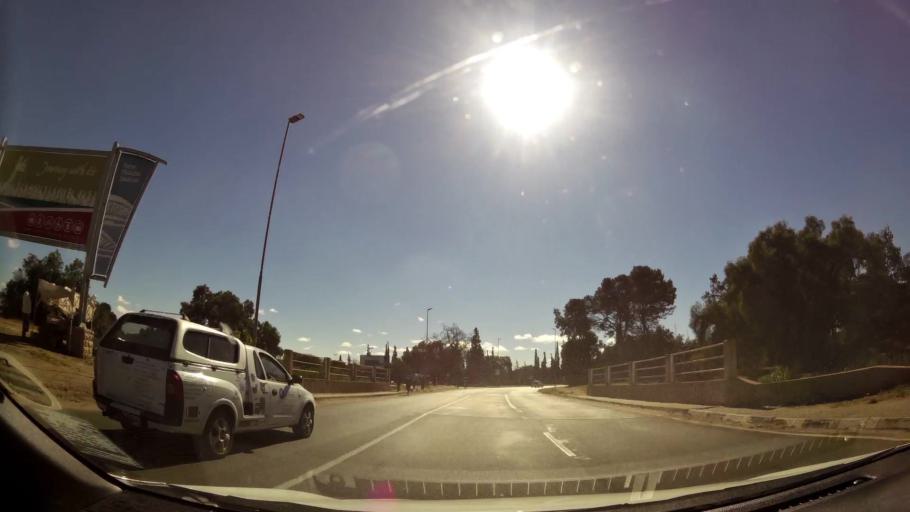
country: ZA
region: Limpopo
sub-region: Capricorn District Municipality
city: Polokwane
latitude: -23.9113
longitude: 29.4450
